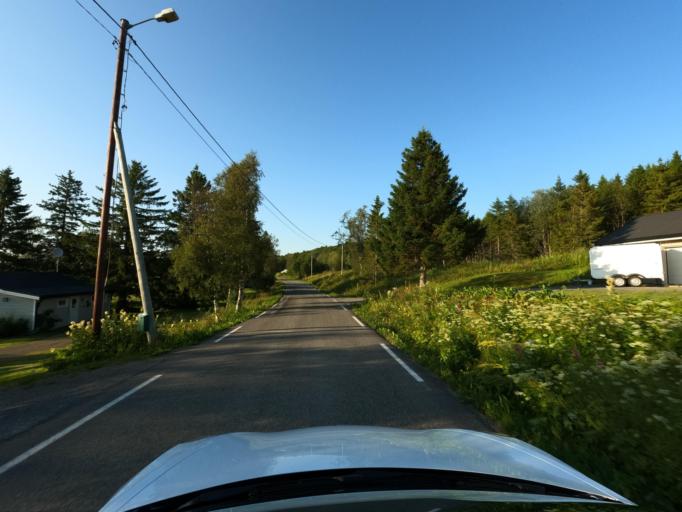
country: NO
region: Nordland
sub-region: Ballangen
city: Ballangen
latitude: 68.4967
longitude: 16.7361
